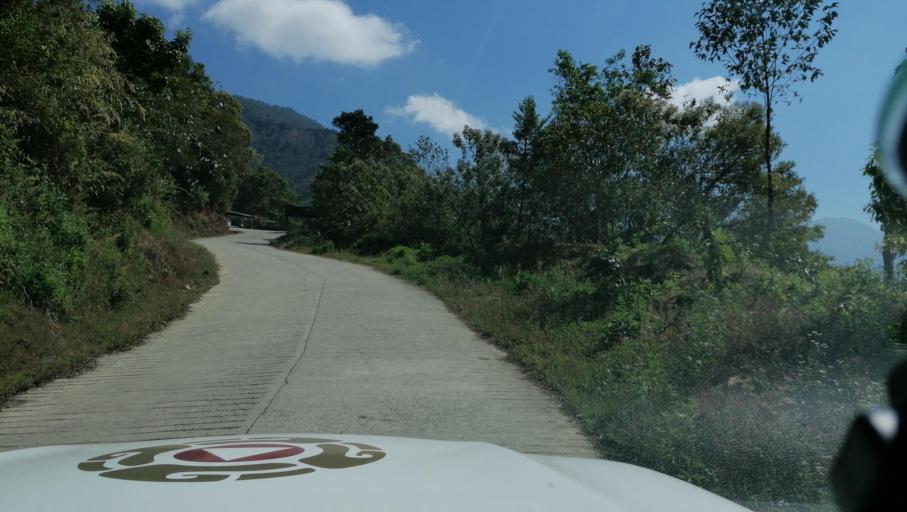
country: GT
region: San Marcos
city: Tacana
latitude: 15.2025
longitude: -92.1999
